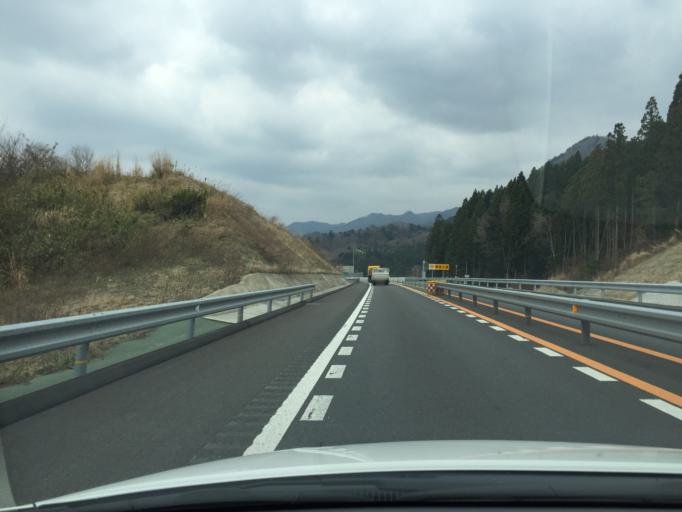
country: JP
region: Miyagi
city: Marumori
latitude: 37.8279
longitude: 140.8758
